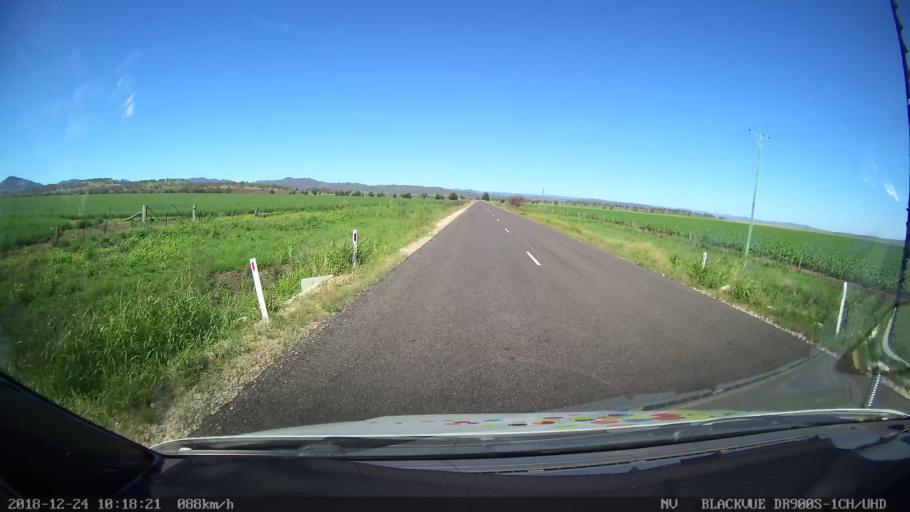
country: AU
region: New South Wales
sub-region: Liverpool Plains
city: Quirindi
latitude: -31.7234
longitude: 150.5777
